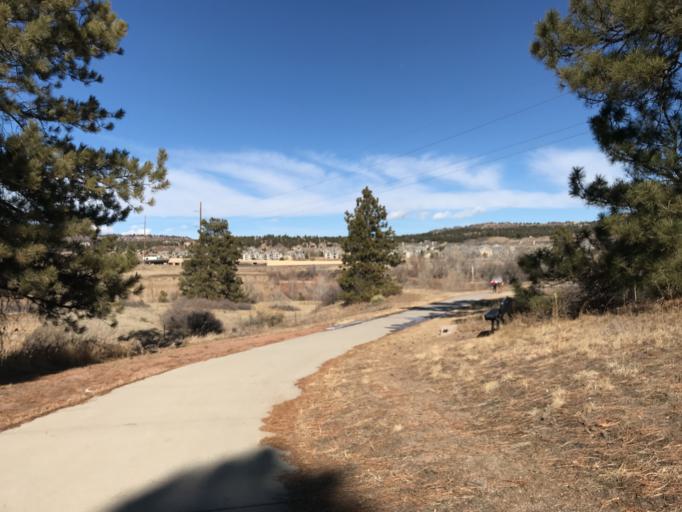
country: US
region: Colorado
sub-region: Douglas County
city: Castle Pines
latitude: 39.4141
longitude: -104.8886
